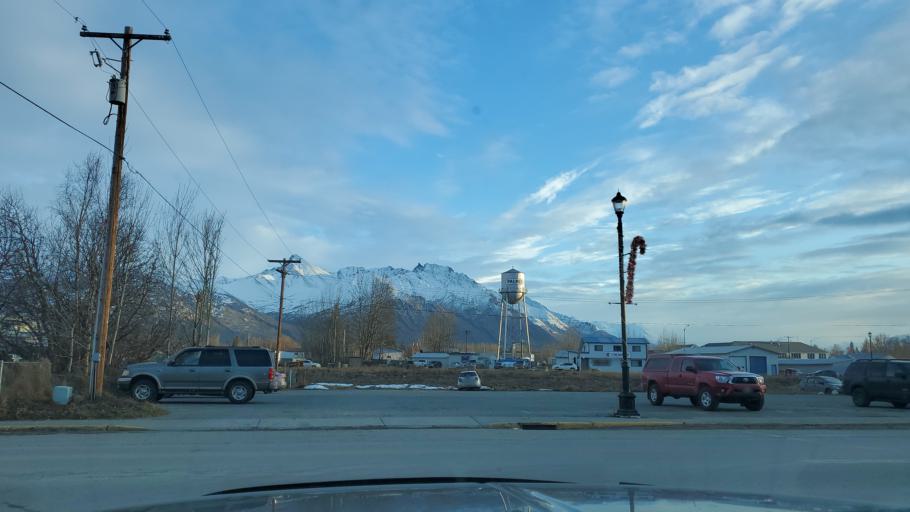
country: US
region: Alaska
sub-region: Matanuska-Susitna Borough
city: Palmer
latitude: 61.6014
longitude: -149.1148
